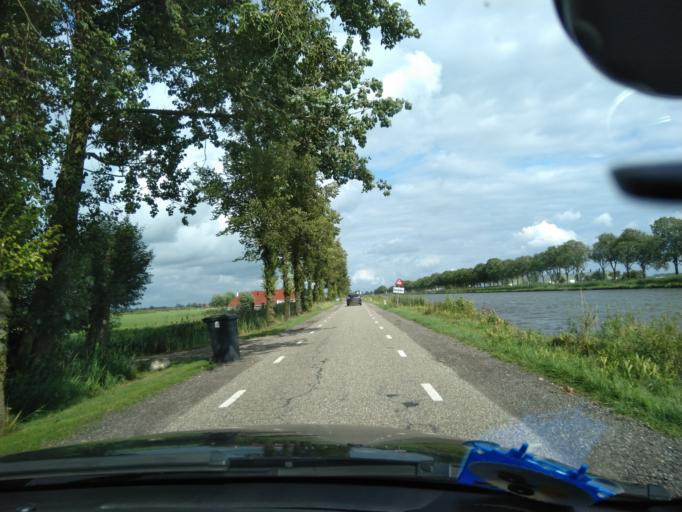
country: NL
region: Groningen
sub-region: Gemeente Zuidhorn
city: Grijpskerk
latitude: 53.2511
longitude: 6.3297
